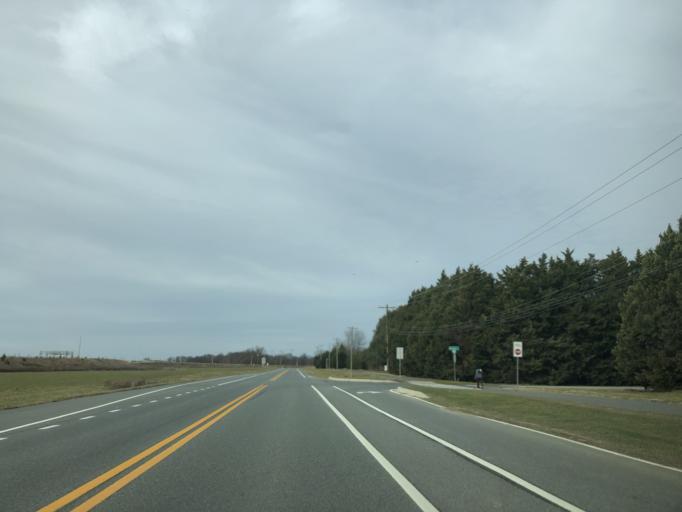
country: US
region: Delaware
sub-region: New Castle County
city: Middletown
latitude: 39.5262
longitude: -75.6728
